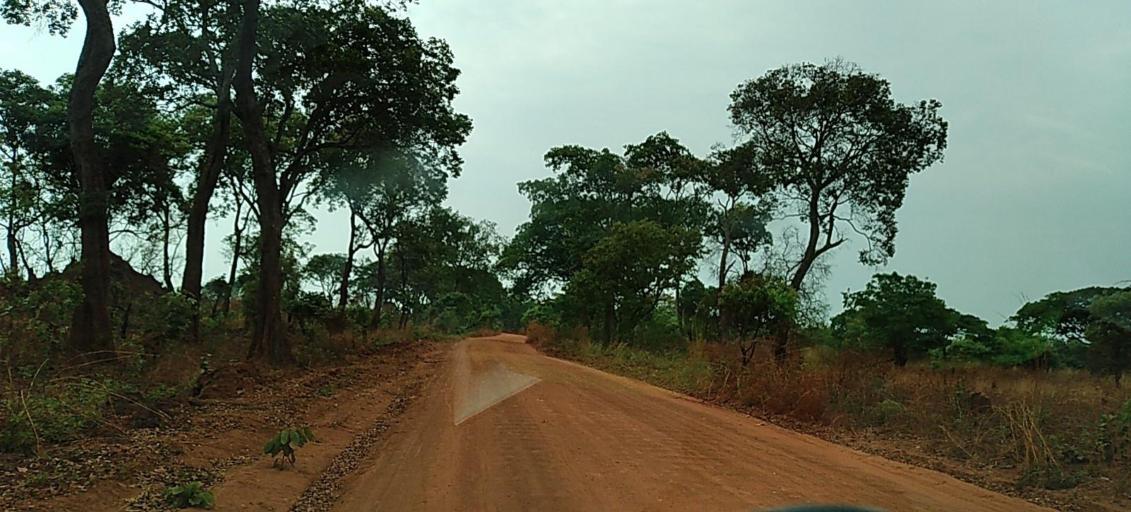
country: ZM
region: North-Western
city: Solwezi
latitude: -12.2098
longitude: 26.5012
